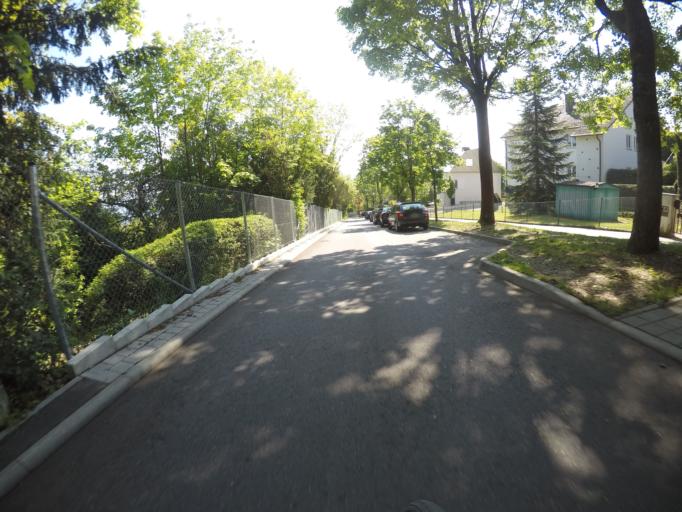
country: DE
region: Baden-Wuerttemberg
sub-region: Regierungsbezirk Stuttgart
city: Stuttgart
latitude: 48.7660
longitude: 9.1530
